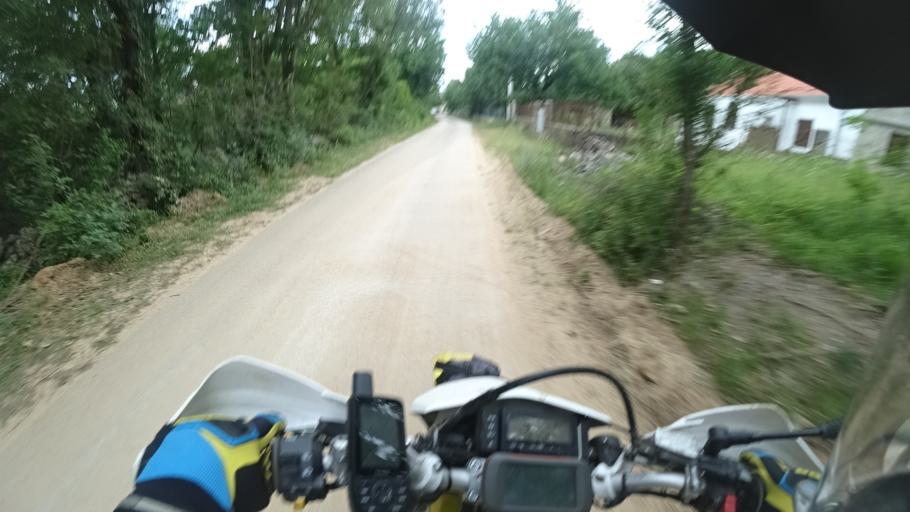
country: HR
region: Sibensko-Kniniska
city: Kistanje
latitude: 44.1073
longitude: 15.9451
